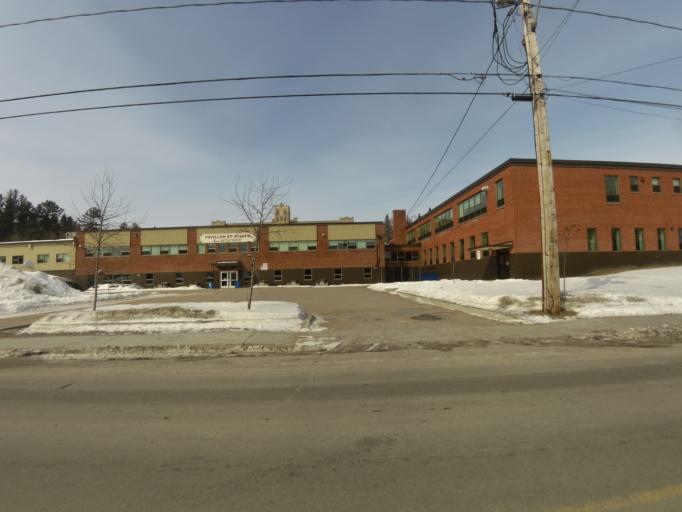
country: CA
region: Quebec
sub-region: Laurentides
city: Mont-Laurier
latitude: 46.5572
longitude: -75.4988
